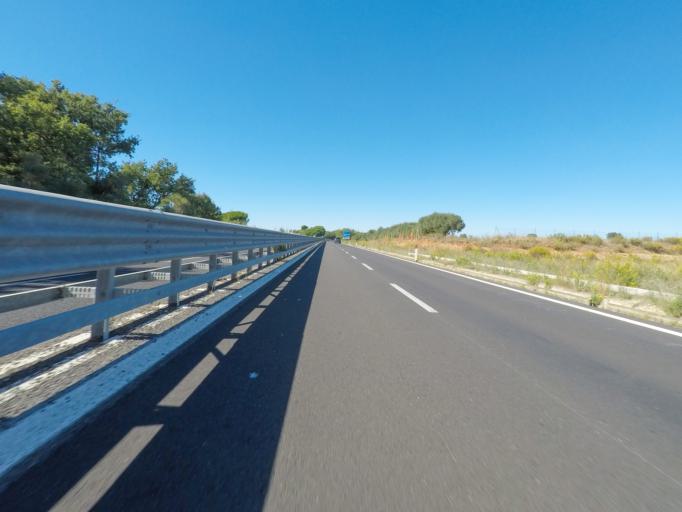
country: IT
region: Latium
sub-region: Provincia di Viterbo
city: Montalto di Castro
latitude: 42.3072
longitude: 11.6592
